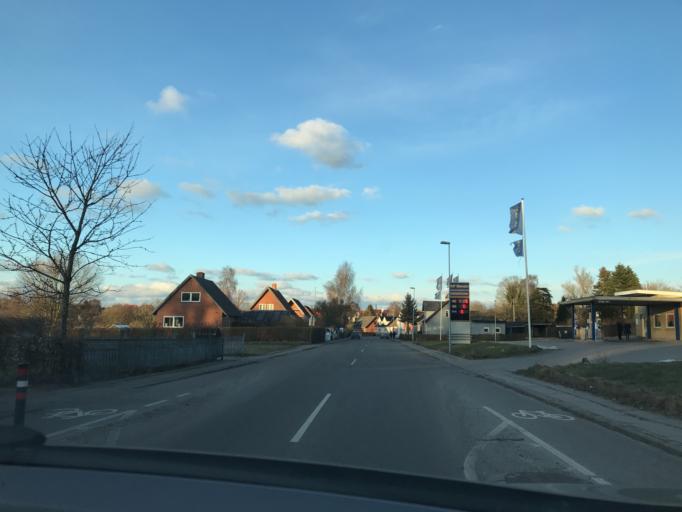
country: DK
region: South Denmark
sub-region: Middelfart Kommune
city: Norre Aby
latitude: 55.4553
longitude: 9.8684
